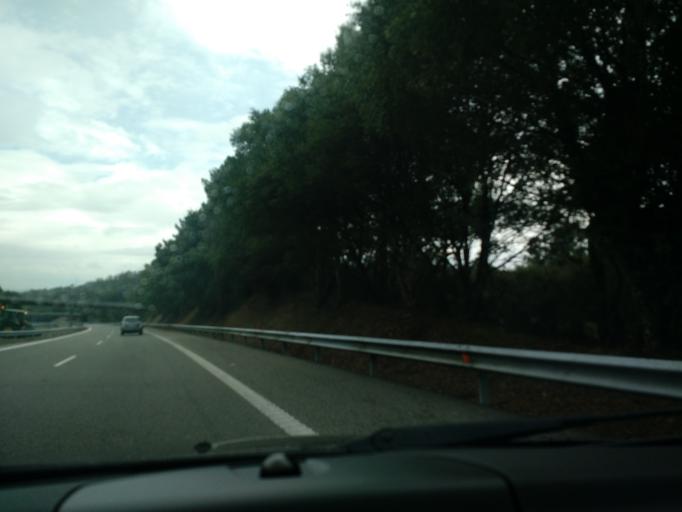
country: ES
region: Galicia
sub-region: Provincia da Coruna
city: Abegondo
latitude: 43.2096
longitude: -8.2805
